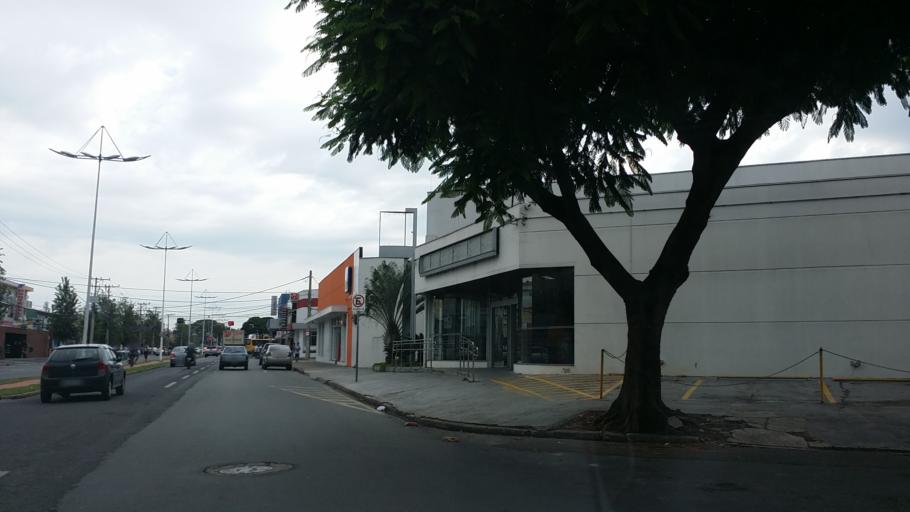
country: BR
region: Sao Paulo
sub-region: Indaiatuba
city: Indaiatuba
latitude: -23.1065
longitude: -47.2182
